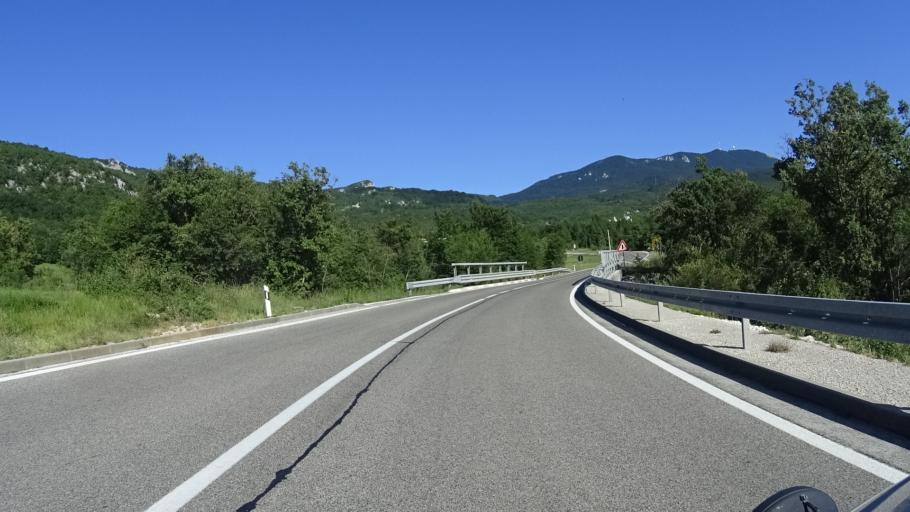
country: HR
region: Istarska
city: Lovran
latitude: 45.3215
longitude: 14.1658
